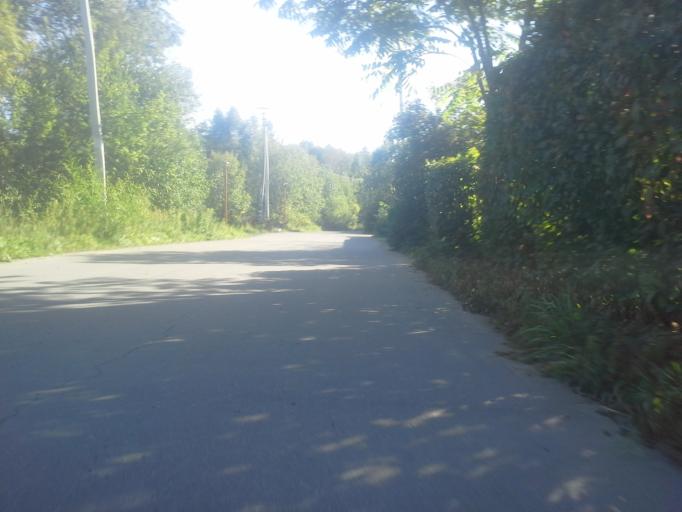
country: RU
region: Moskovskaya
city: Kievskij
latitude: 55.3511
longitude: 36.9491
